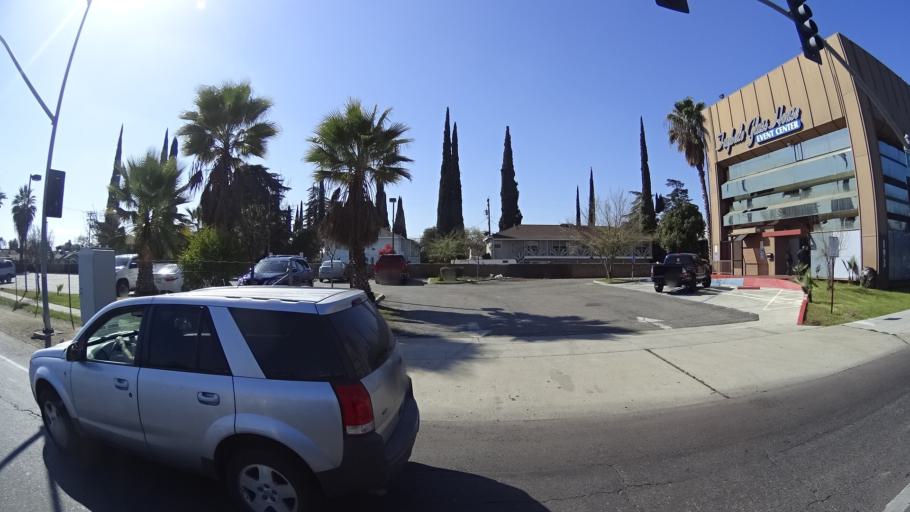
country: US
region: California
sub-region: Fresno County
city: Fresno
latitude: 36.7796
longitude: -119.7871
